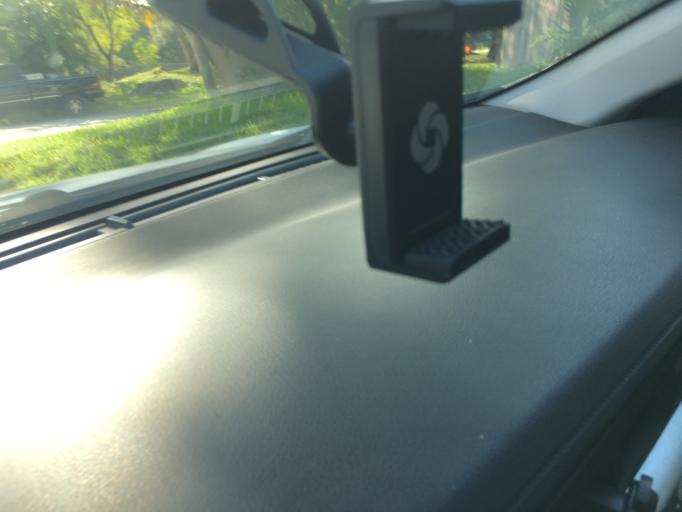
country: US
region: Florida
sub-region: Broward County
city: Dania Beach
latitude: 26.0703
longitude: -80.1697
